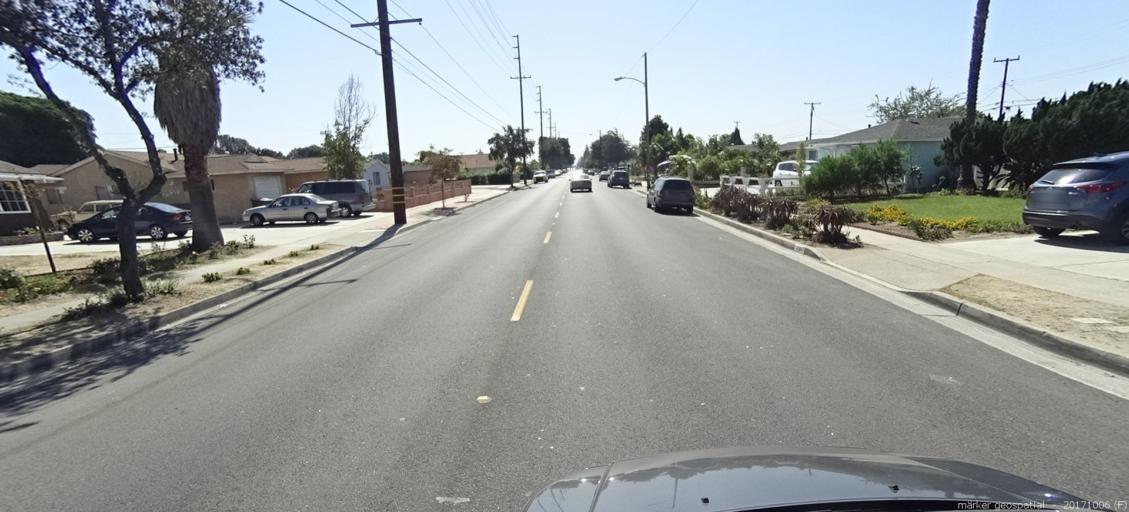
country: US
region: California
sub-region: Orange County
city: Stanton
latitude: 33.7949
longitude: -117.9842
